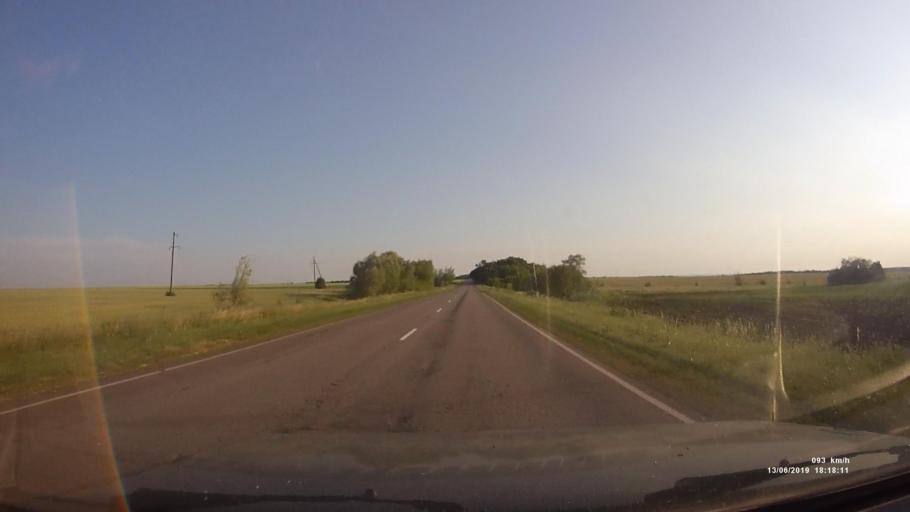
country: RU
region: Rostov
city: Kazanskaya
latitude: 49.9109
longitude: 41.3166
